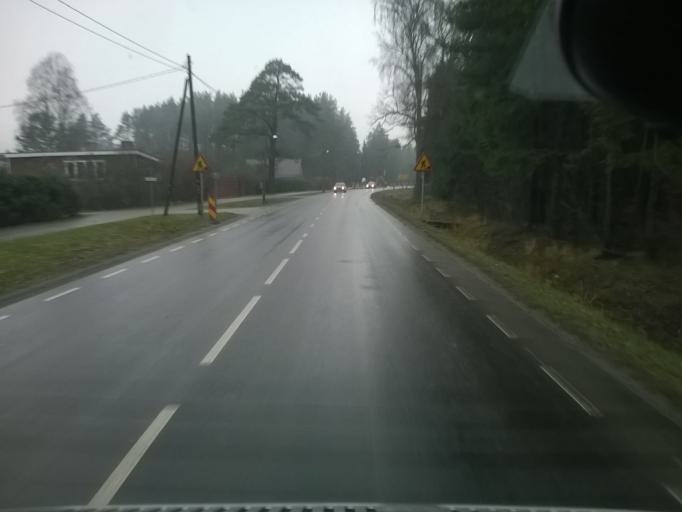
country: EE
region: Harju
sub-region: Saku vald
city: Saku
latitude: 59.2421
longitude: 24.6804
